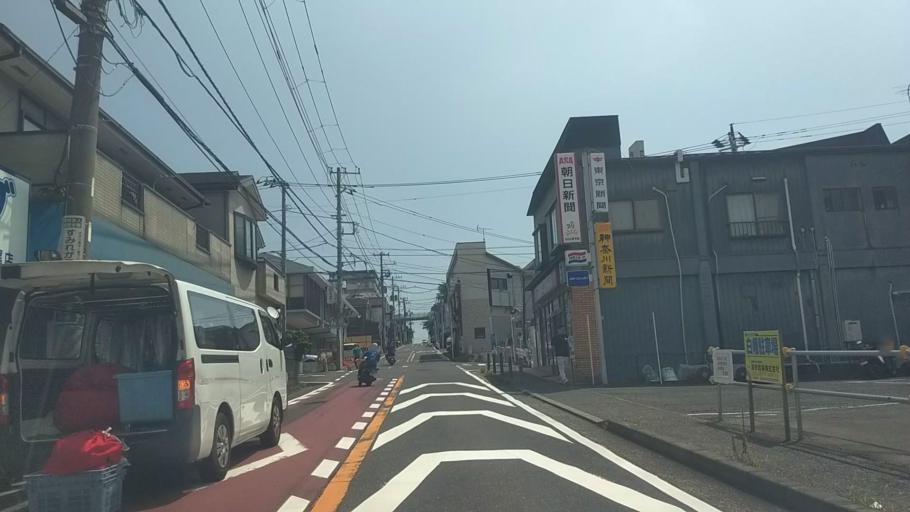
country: JP
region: Kanagawa
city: Yokohama
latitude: 35.5010
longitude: 139.6552
